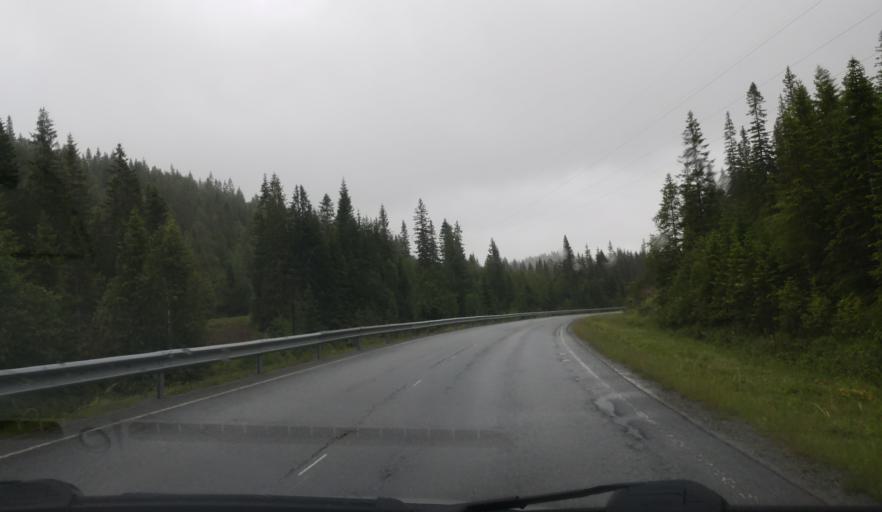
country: NO
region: Sor-Trondelag
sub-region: Selbu
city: Mebonden
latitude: 63.3363
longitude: 11.0932
